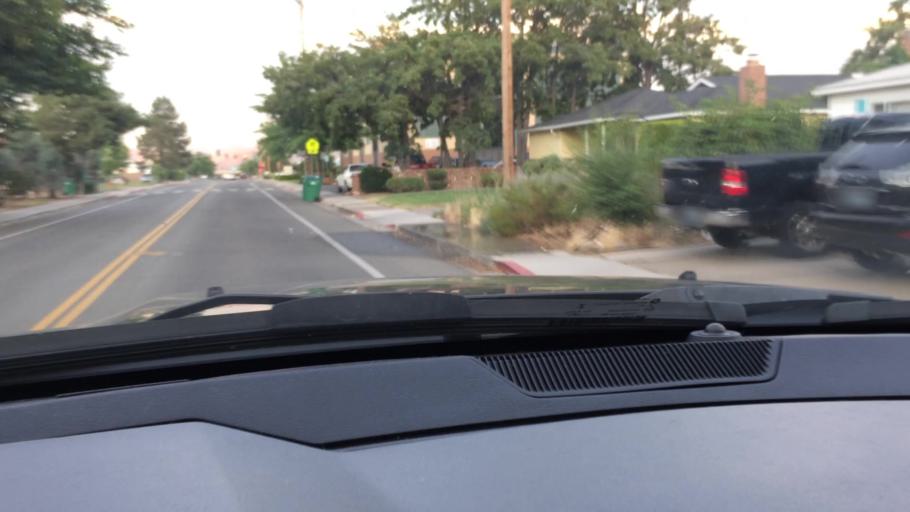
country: US
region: Nevada
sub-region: Washoe County
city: Reno
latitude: 39.5129
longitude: -119.7921
